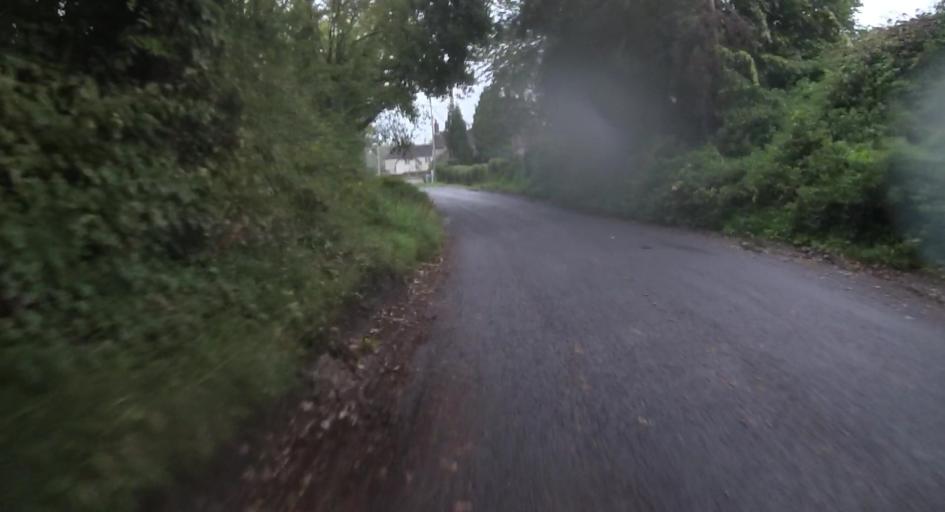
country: GB
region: England
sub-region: West Berkshire
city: Thatcham
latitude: 51.3983
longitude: -1.2080
